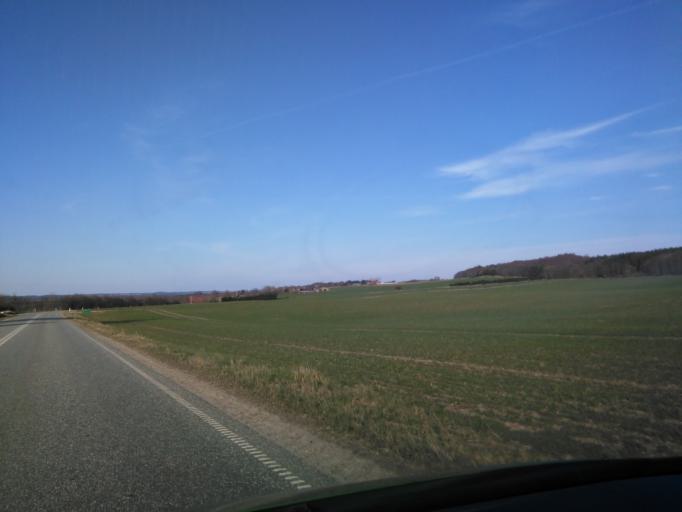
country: DK
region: Central Jutland
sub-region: Skanderborg Kommune
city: Ry
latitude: 56.0019
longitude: 9.7719
